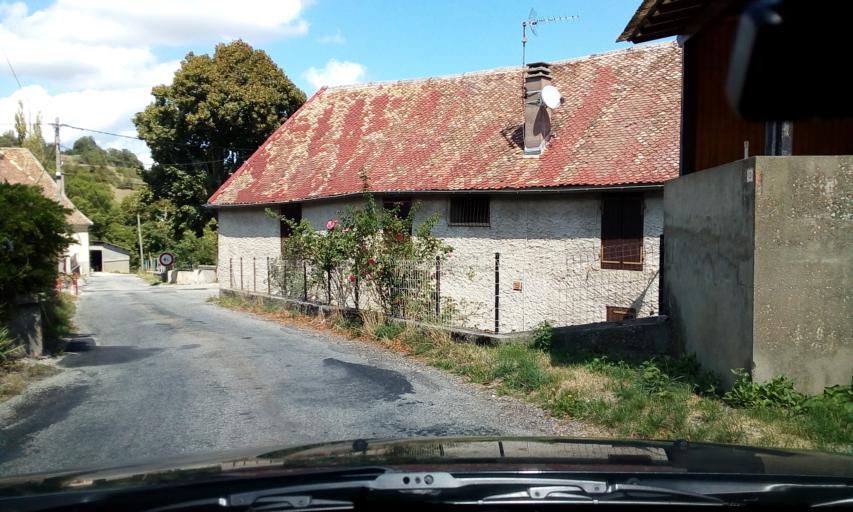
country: FR
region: Rhone-Alpes
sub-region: Departement de l'Isere
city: Mens
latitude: 44.7646
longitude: 5.6644
